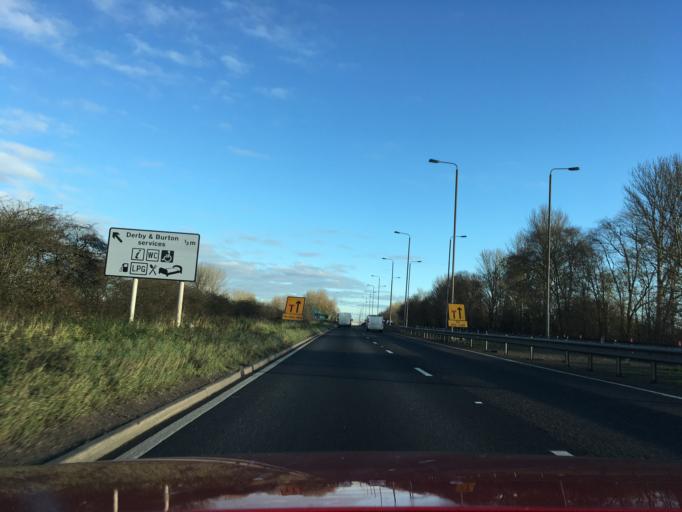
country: GB
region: England
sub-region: Derbyshire
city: Etwall
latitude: 52.8578
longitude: -1.5788
